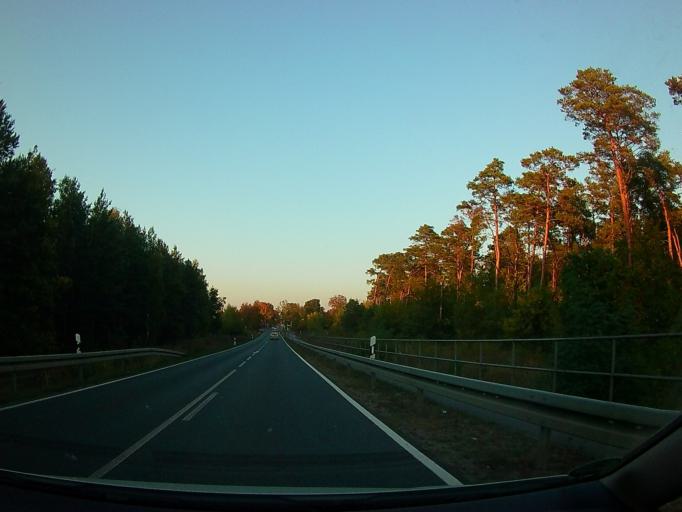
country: DE
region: Berlin
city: Bohnsdorf
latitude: 52.3875
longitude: 13.5698
